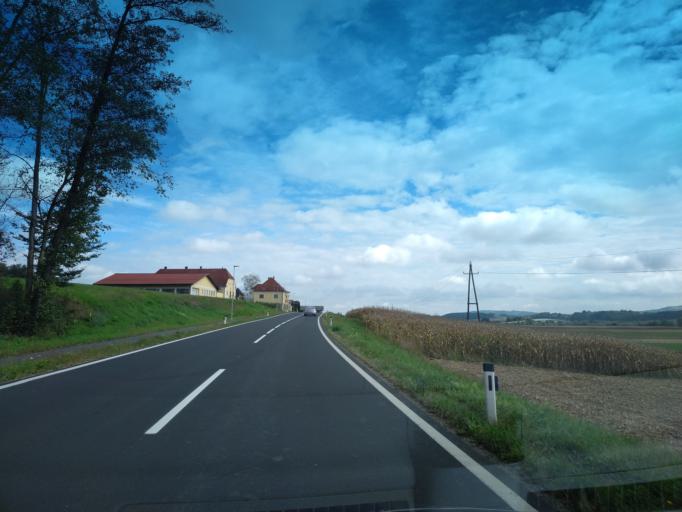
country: AT
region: Styria
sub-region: Politischer Bezirk Deutschlandsberg
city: Gross Sankt Florian
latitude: 46.8290
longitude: 15.3358
